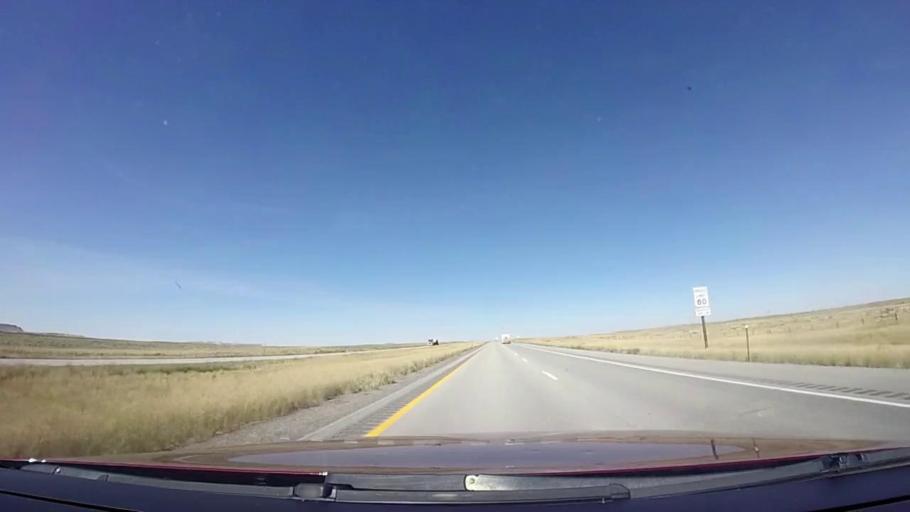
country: US
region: Wyoming
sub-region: Sweetwater County
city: Rock Springs
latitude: 41.6311
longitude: -108.3276
